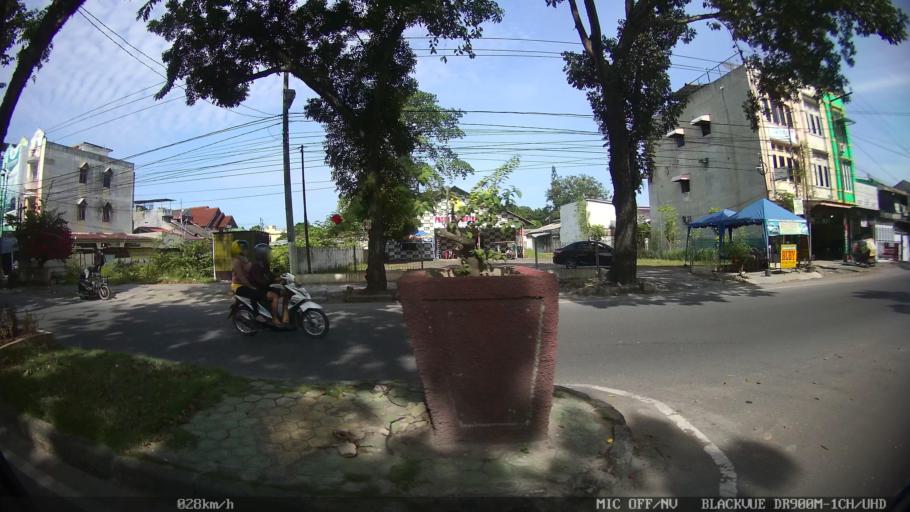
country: ID
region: North Sumatra
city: Medan
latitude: 3.5814
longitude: 98.6433
